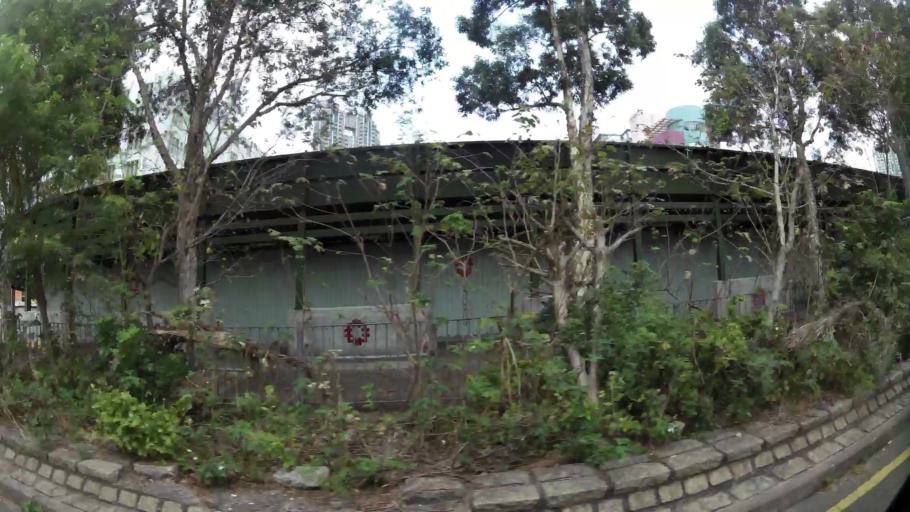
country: HK
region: Sham Shui Po
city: Sham Shui Po
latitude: 22.3304
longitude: 114.1509
